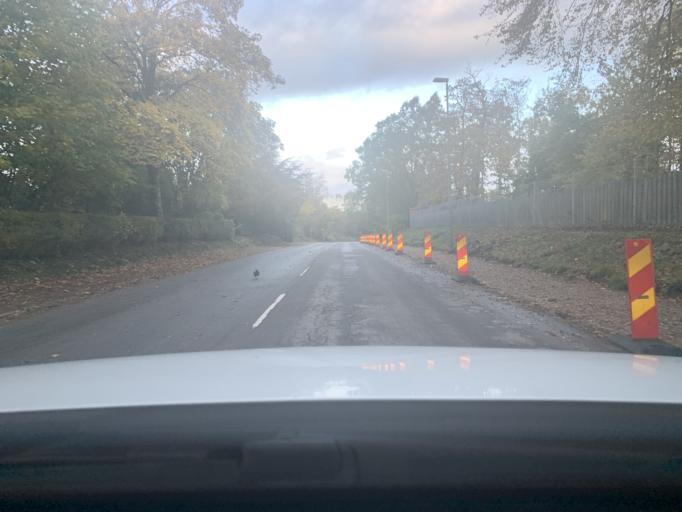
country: SE
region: Skane
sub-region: Horby Kommun
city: Hoerby
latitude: 55.8418
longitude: 13.6561
